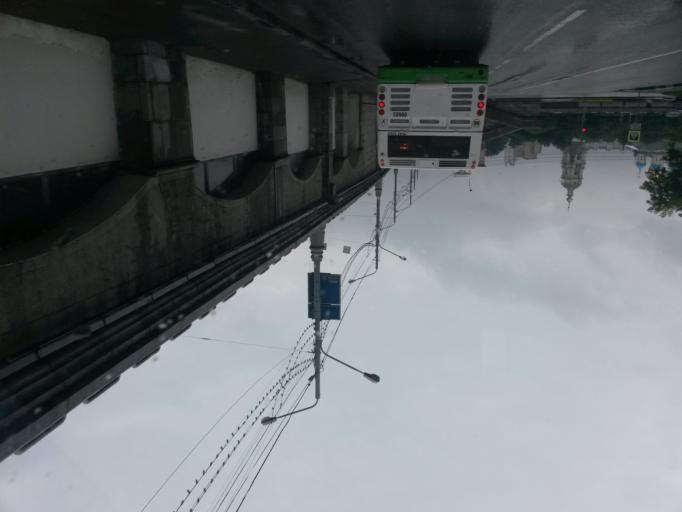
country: RU
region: Moscow
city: Taganskiy
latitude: 55.7281
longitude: 37.6520
